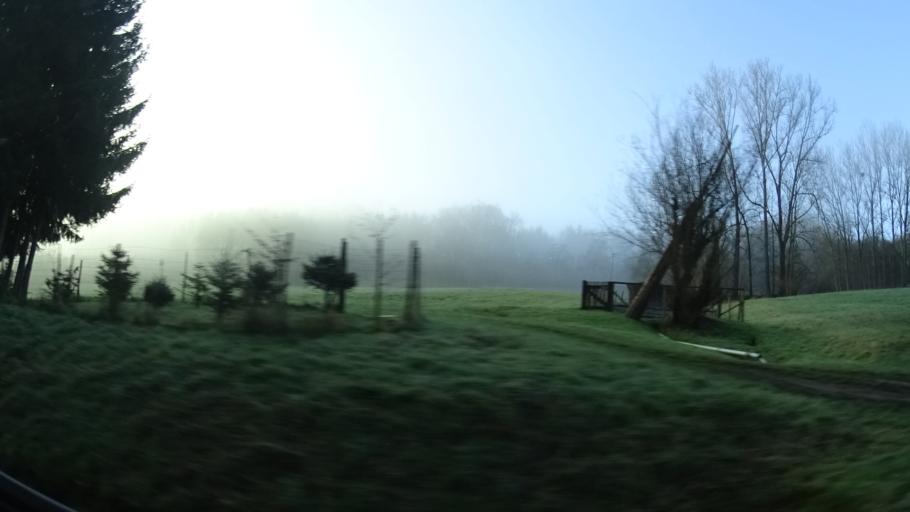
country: DE
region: Bavaria
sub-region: Regierungsbezirk Unterfranken
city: Eichenbuhl
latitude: 49.6655
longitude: 9.3640
